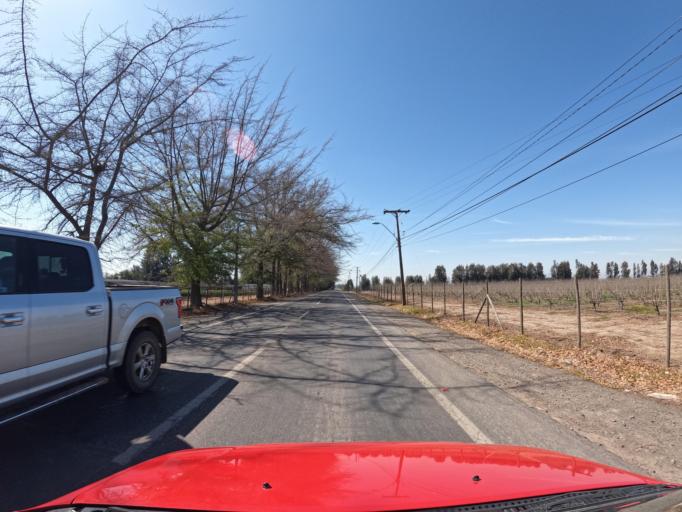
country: CL
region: Maule
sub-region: Provincia de Curico
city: Rauco
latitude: -34.9969
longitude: -71.3679
